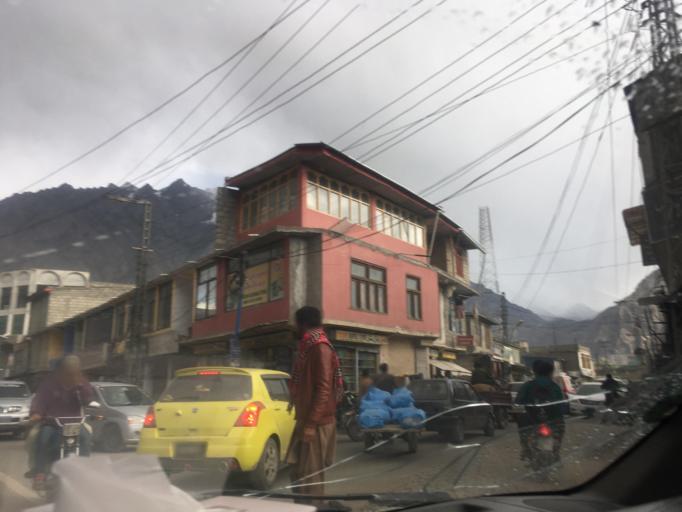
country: PK
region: Gilgit-Baltistan
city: Skardu
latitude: 35.3000
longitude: 75.6337
